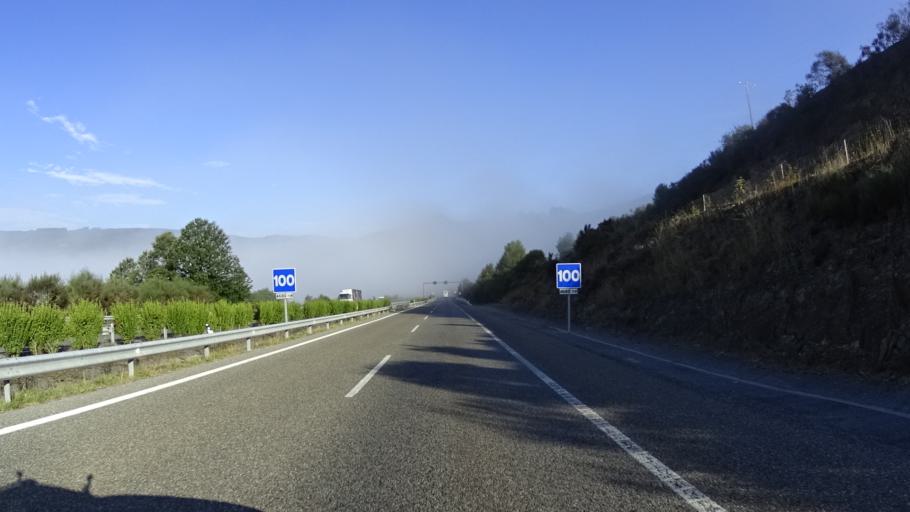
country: ES
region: Galicia
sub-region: Provincia de Lugo
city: San Roman
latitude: 42.7778
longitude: -7.0982
